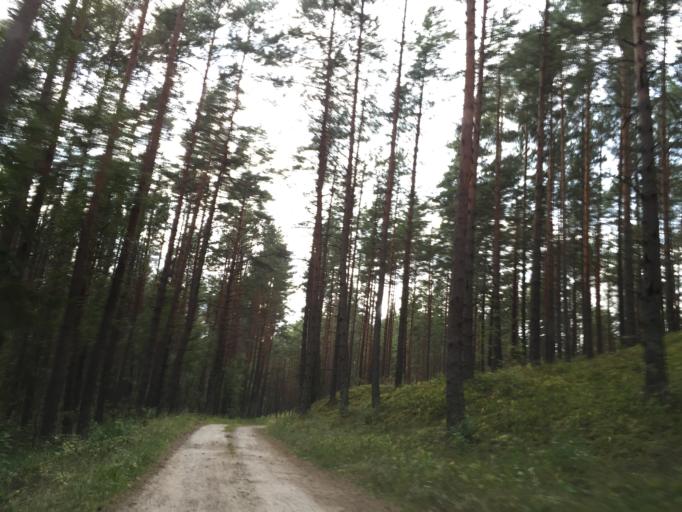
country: LV
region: Jurmala
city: Jurmala
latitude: 56.8759
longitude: 23.7333
